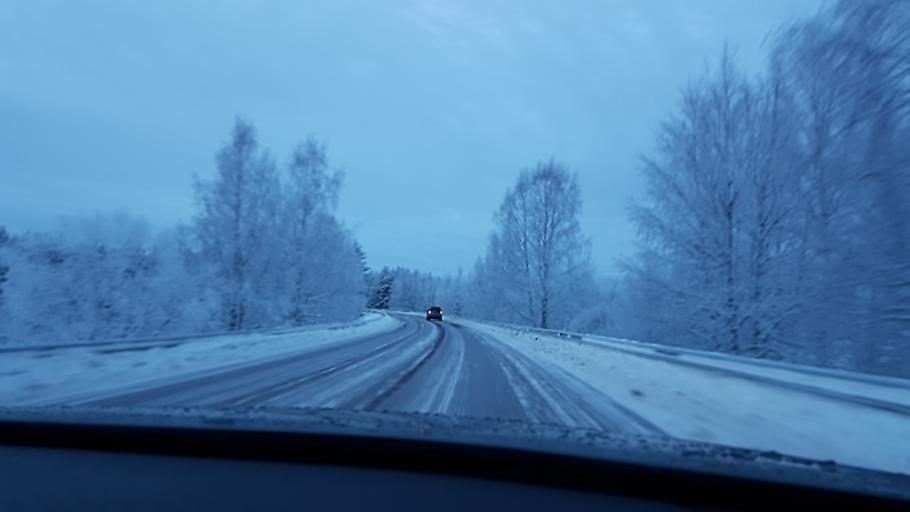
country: SE
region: Jaemtland
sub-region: Harjedalens Kommun
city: Sveg
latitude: 62.0516
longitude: 14.6412
